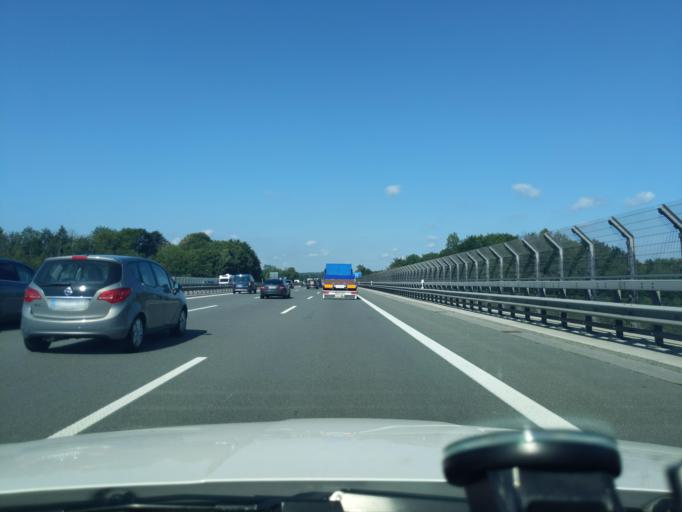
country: DE
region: Bavaria
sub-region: Upper Bavaria
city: Weyarn
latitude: 47.8694
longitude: 11.7871
